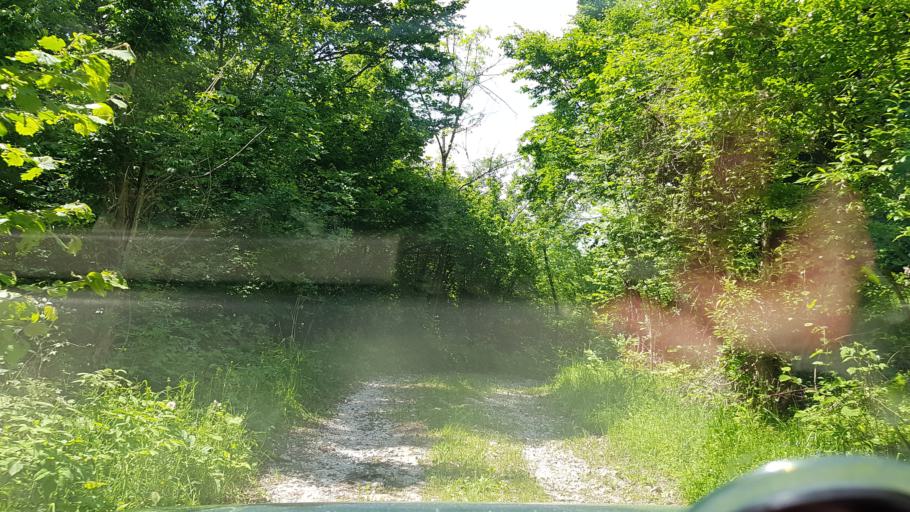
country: IT
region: Friuli Venezia Giulia
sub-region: Provincia di Udine
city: Pulfero
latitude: 46.1944
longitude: 13.4244
